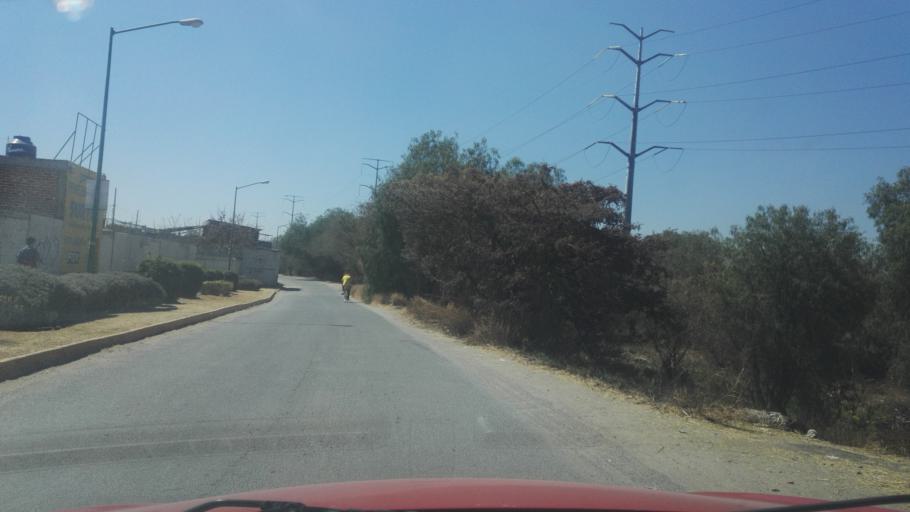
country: MX
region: Guanajuato
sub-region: Leon
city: Fraccionamiento Paraiso Real
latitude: 21.0837
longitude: -101.5943
